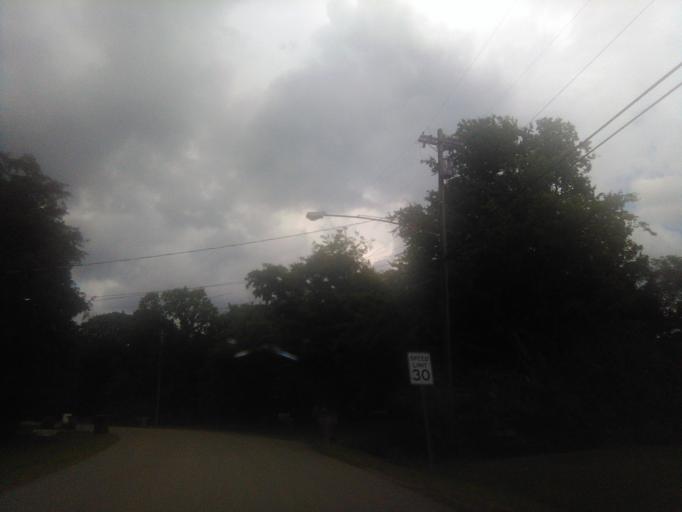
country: US
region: Tennessee
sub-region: Davidson County
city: Belle Meade
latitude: 36.0998
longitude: -86.8316
